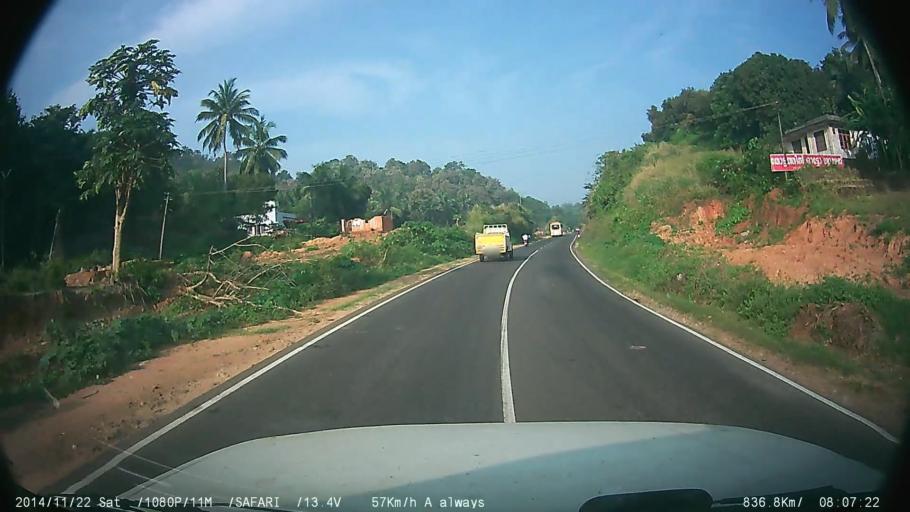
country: IN
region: Kerala
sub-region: Thrissur District
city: Chelakara
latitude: 10.5918
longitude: 76.4651
